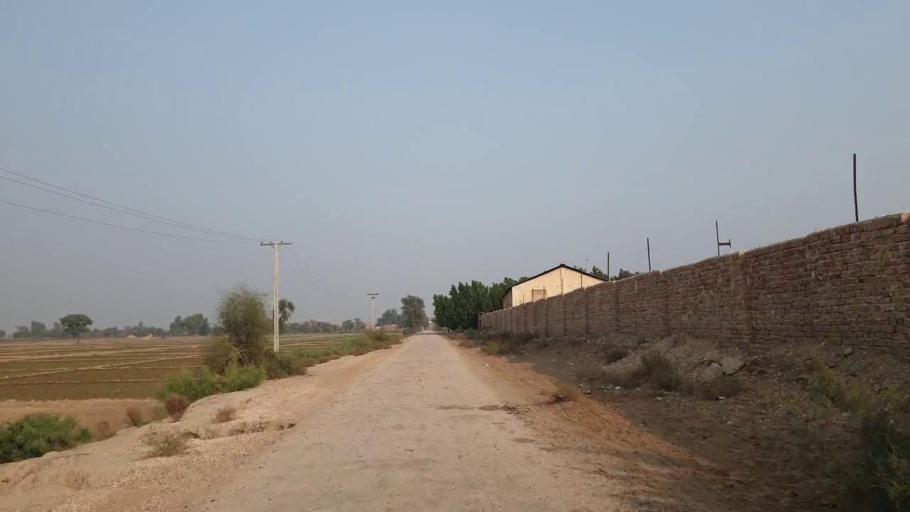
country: PK
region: Sindh
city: Bhan
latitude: 26.4888
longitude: 67.7250
